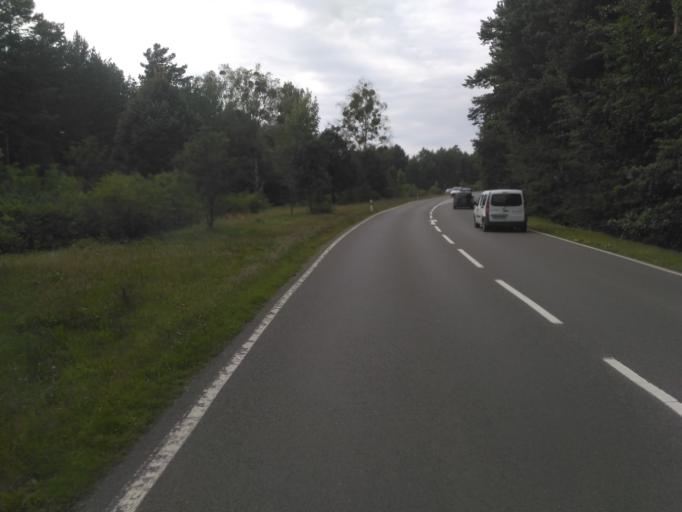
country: DE
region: Saxony
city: Bernsdorf
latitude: 51.4450
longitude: 14.1214
